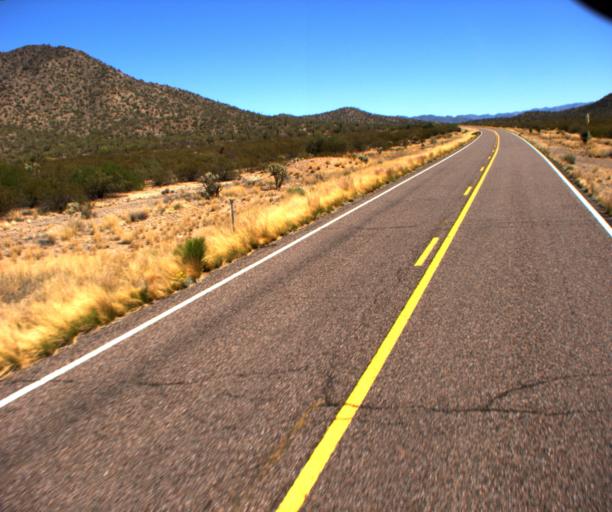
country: US
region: Arizona
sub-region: Yavapai County
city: Congress
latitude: 34.0931
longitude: -113.0047
